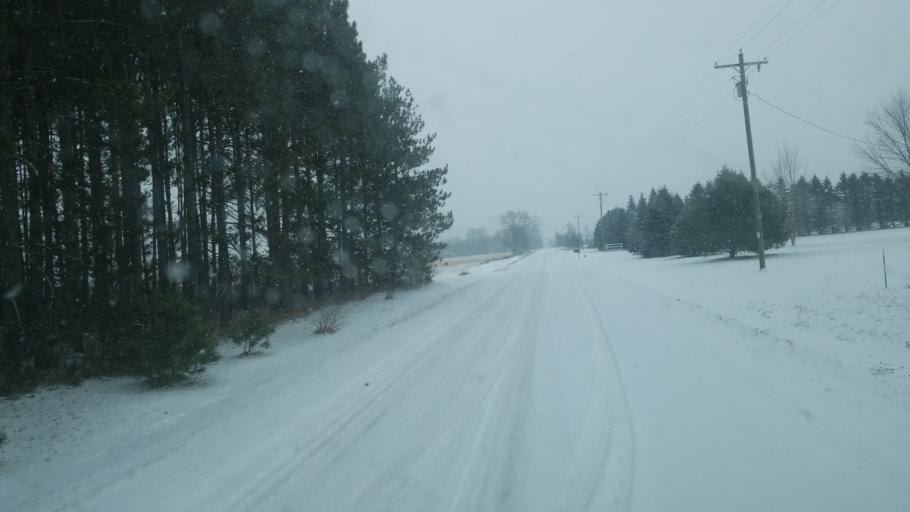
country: US
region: Michigan
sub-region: Osceola County
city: Reed City
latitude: 43.8233
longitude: -85.4140
